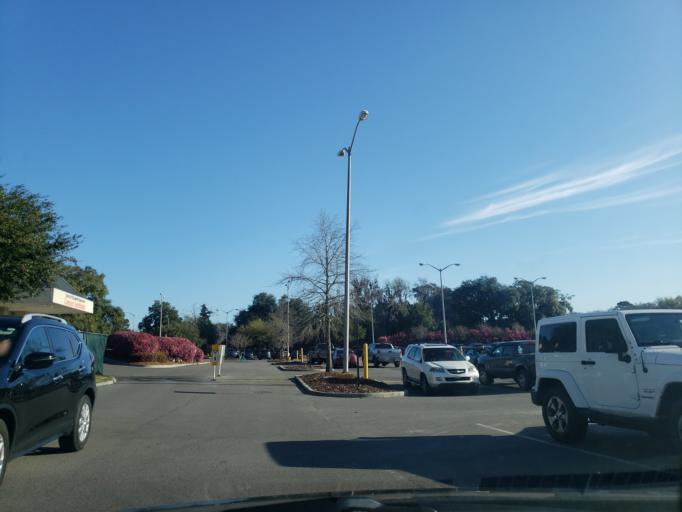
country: US
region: Georgia
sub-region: Chatham County
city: Thunderbolt
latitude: 32.0299
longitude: -81.0870
